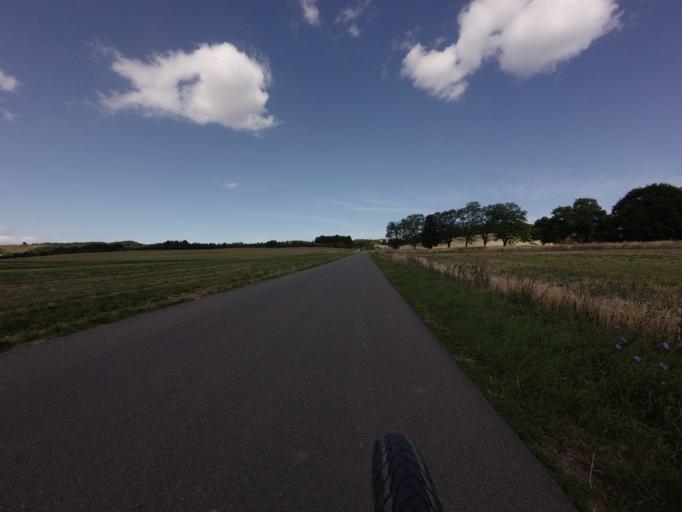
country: DK
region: Zealand
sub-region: Vordingborg Kommune
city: Stege
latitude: 54.9531
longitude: 12.5328
